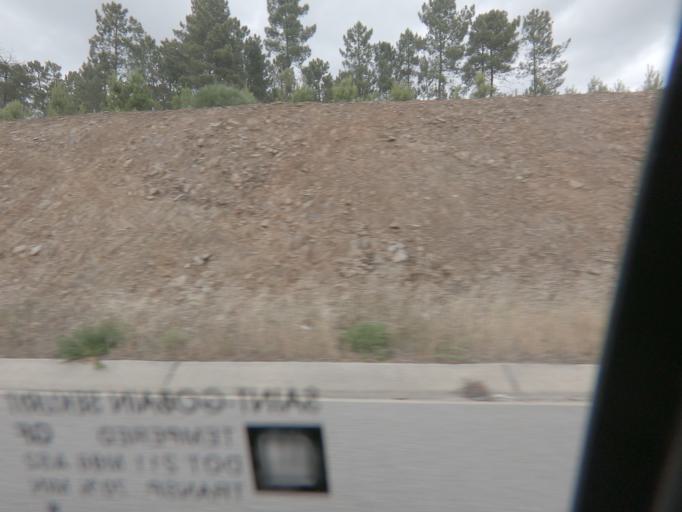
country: PT
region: Vila Real
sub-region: Vila Real
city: Vila Real
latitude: 41.2712
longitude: -7.6915
